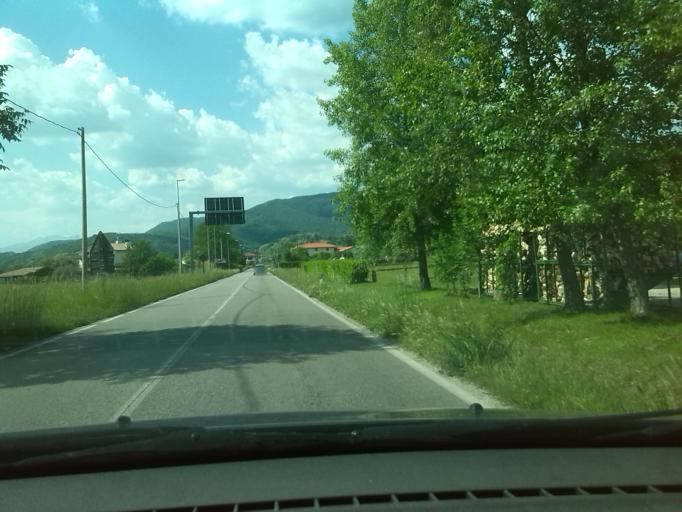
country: IT
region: Friuli Venezia Giulia
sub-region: Provincia di Udine
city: Cividale del Friuli
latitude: 46.1052
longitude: 13.4155
